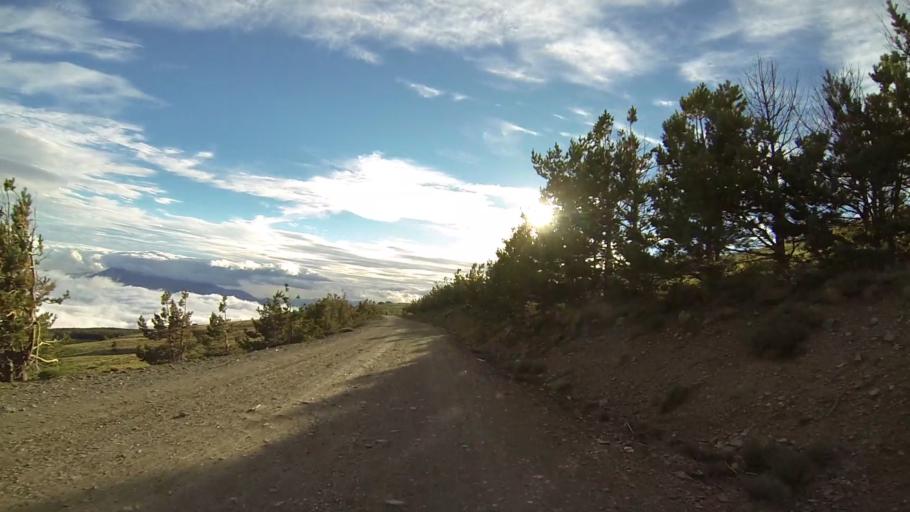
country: ES
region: Andalusia
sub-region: Provincia de Granada
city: Portugos
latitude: 36.9820
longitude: -3.3211
